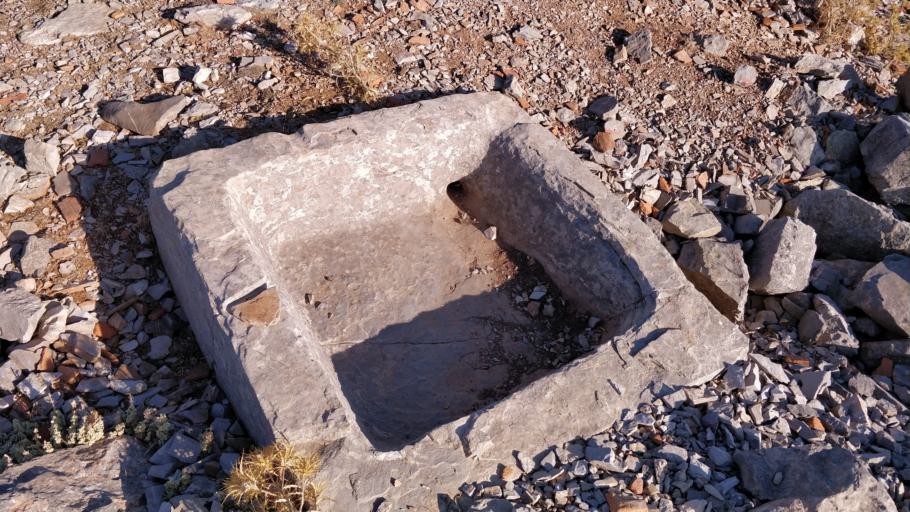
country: GR
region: South Aegean
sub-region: Nomos Dodekanisou
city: Emponas
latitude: 36.2067
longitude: 27.8644
